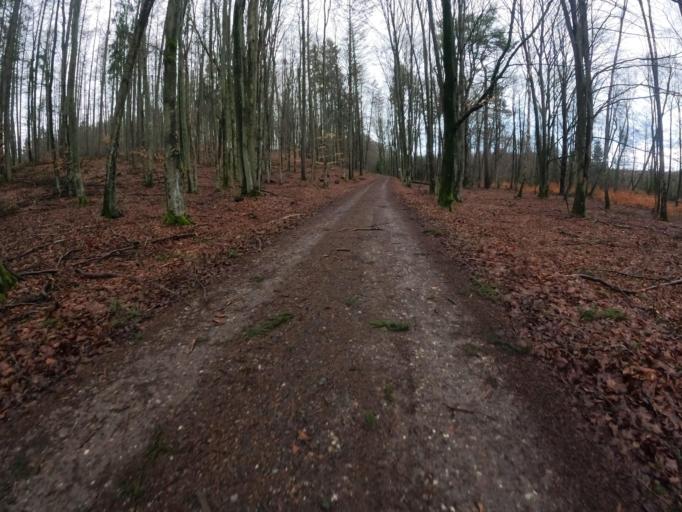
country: PL
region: West Pomeranian Voivodeship
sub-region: Powiat slawienski
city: Slawno
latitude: 54.2674
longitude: 16.7182
